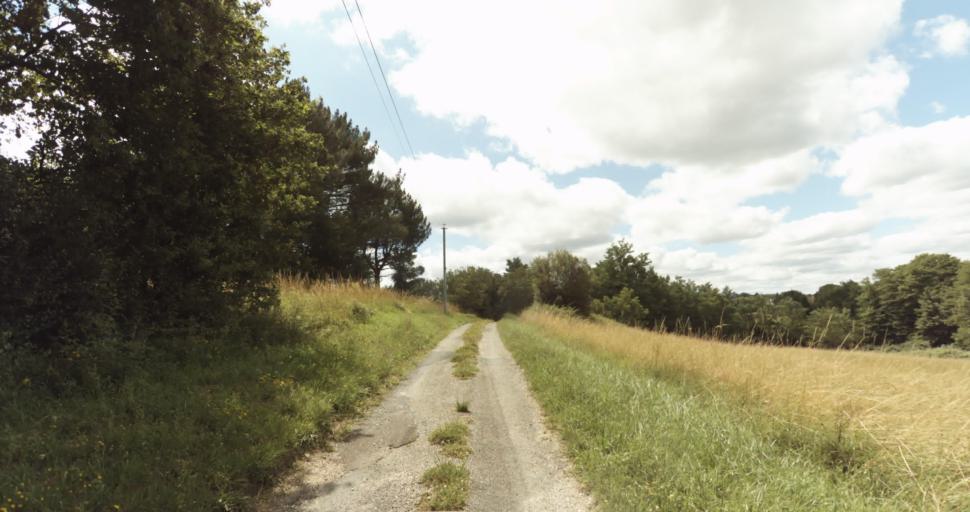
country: FR
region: Aquitaine
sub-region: Departement de la Gironde
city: Bazas
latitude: 44.4390
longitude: -0.2165
